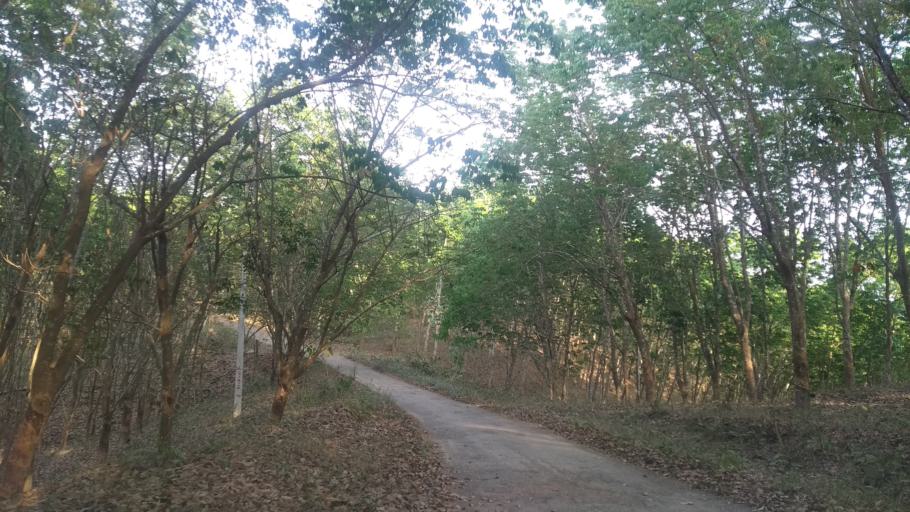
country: IN
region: Tripura
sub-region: West Tripura
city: Sonamura
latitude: 23.4440
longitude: 91.3673
